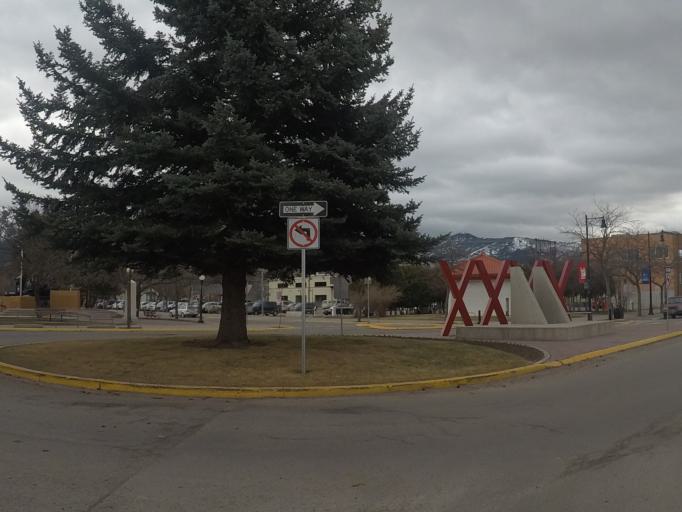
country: US
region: Montana
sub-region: Missoula County
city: Missoula
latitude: 46.8753
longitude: -113.9921
